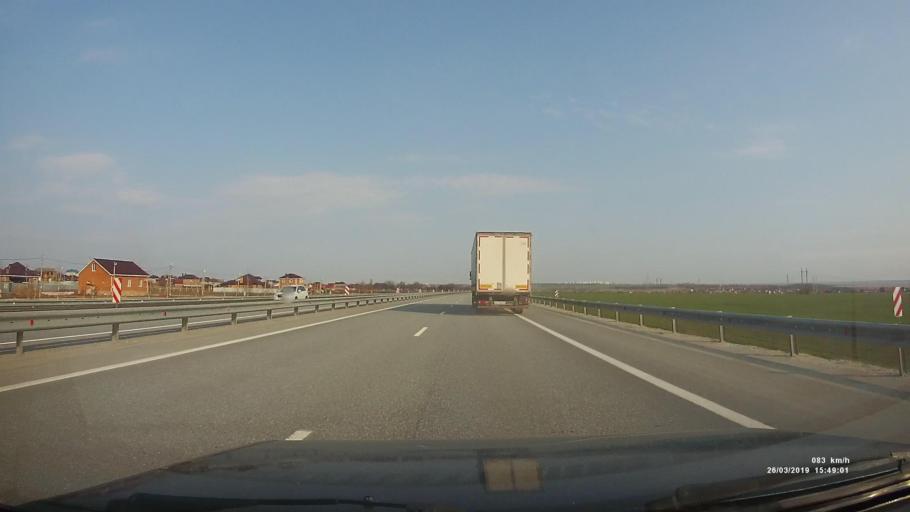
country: RU
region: Rostov
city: Chaltyr
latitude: 47.2774
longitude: 39.4625
